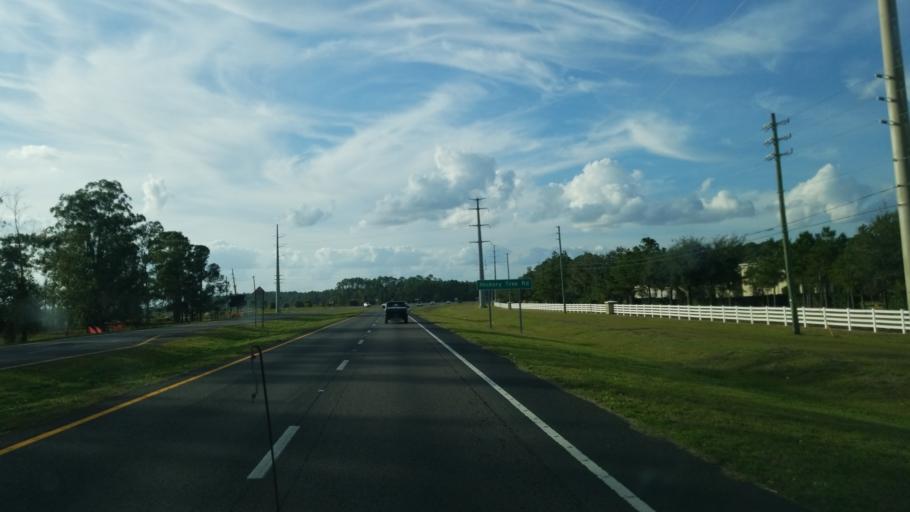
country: US
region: Florida
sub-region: Osceola County
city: Saint Cloud
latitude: 28.1951
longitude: -81.1608
